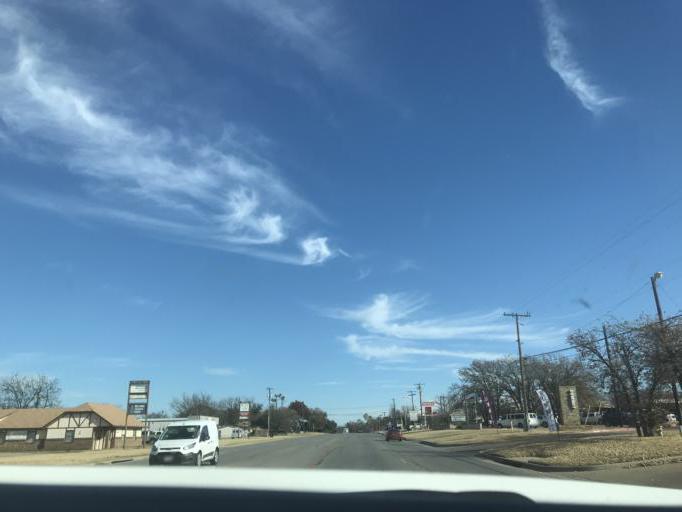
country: US
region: Texas
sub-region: Erath County
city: Stephenville
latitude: 32.2256
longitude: -98.2296
